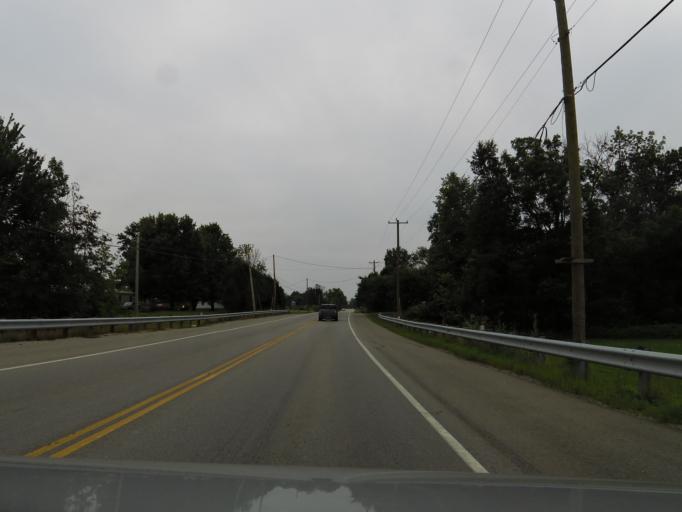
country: US
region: Ohio
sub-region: Brown County
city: Mount Orab
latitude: 39.0619
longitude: -83.9244
